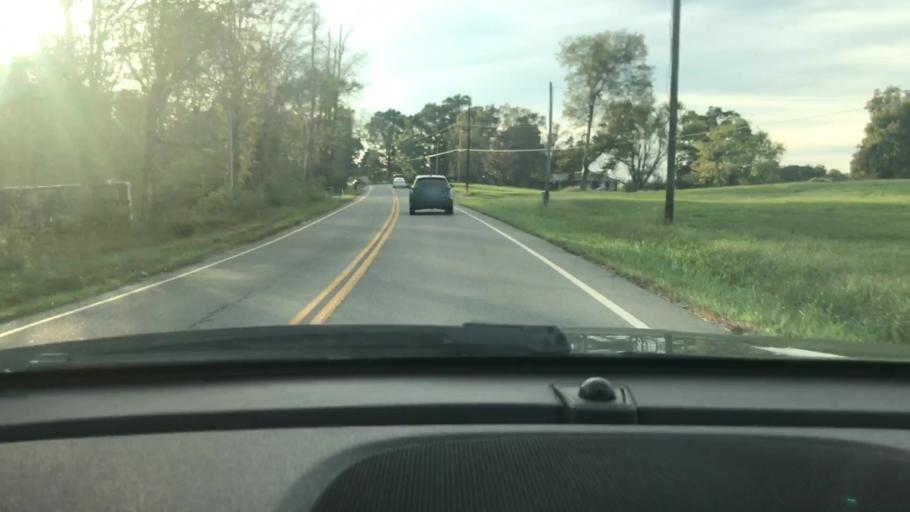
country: US
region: Tennessee
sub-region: Cheatham County
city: Ashland City
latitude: 36.2695
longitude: -87.2116
